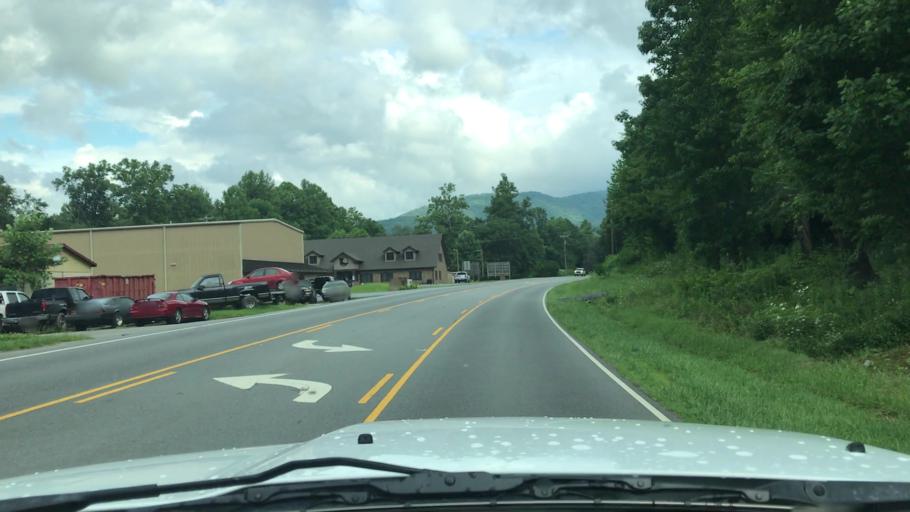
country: US
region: North Carolina
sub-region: Graham County
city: Robbinsville
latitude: 35.3105
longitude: -83.7954
